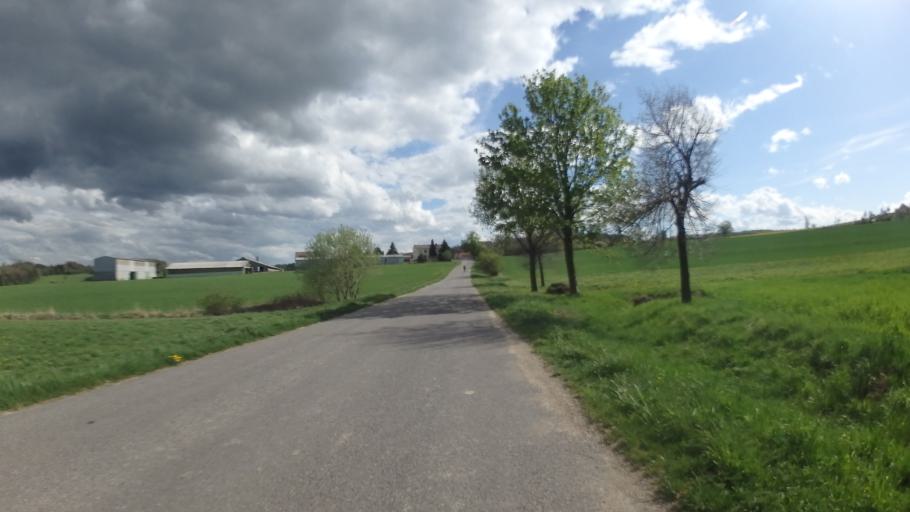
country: CZ
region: Vysocina
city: Merin
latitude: 49.3537
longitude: 15.8785
